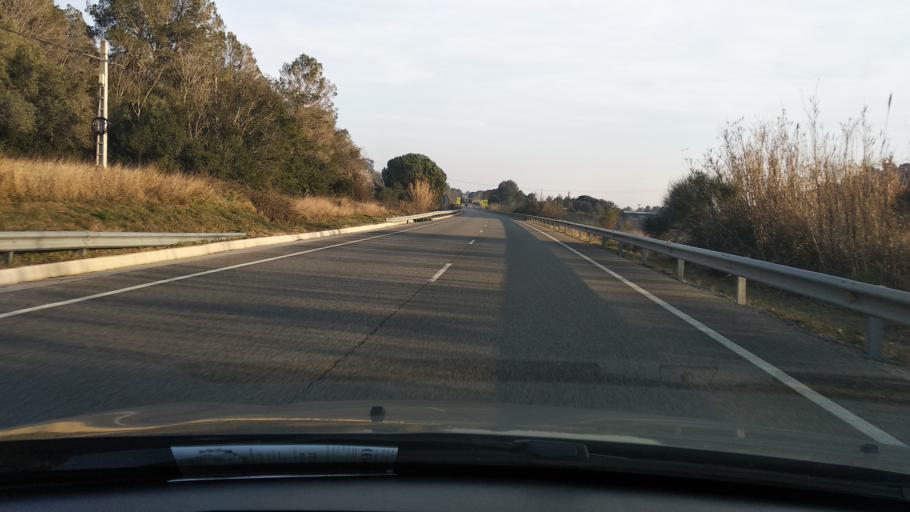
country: ES
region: Catalonia
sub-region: Provincia de Tarragona
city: les Borges del Camp
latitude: 41.1857
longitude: 1.0051
